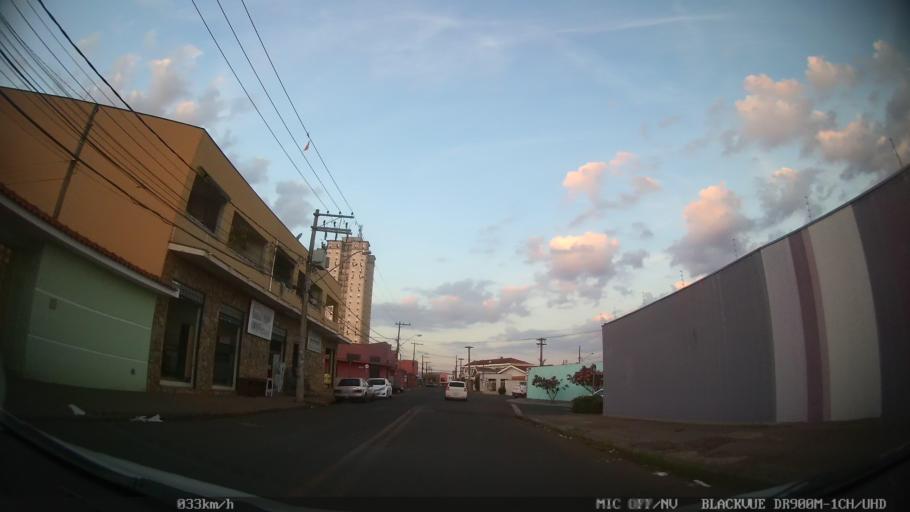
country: BR
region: Sao Paulo
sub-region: Ribeirao Preto
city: Ribeirao Preto
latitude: -21.1568
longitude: -47.8308
